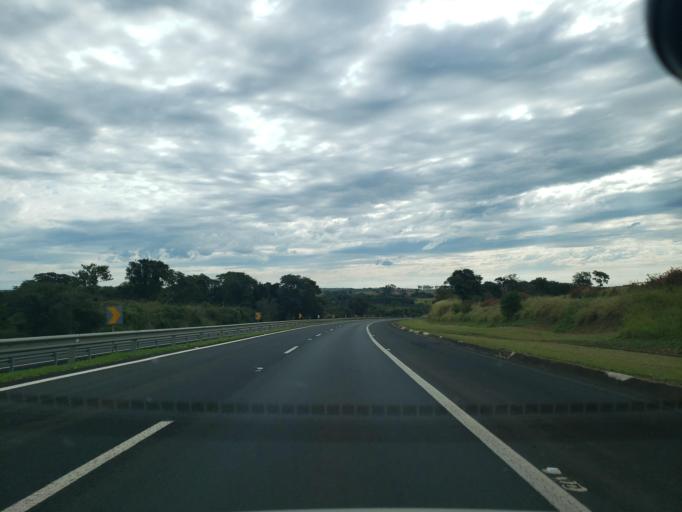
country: BR
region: Sao Paulo
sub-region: Bauru
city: Bauru
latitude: -22.2112
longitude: -49.1791
